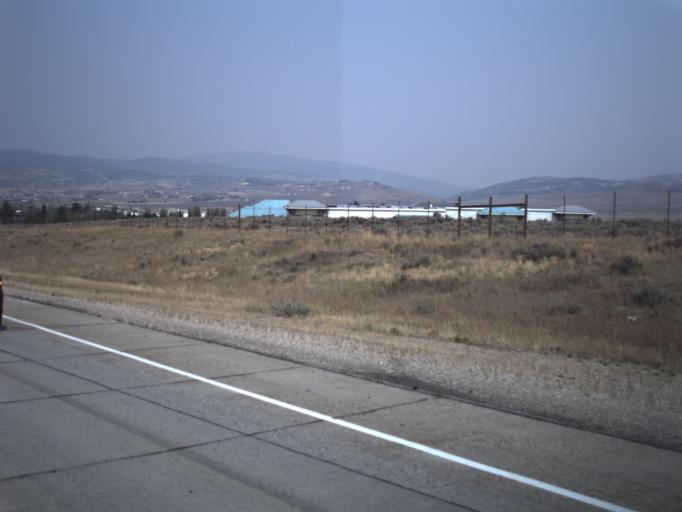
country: US
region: Utah
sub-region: Summit County
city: Snyderville
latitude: 40.7140
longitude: -111.4839
